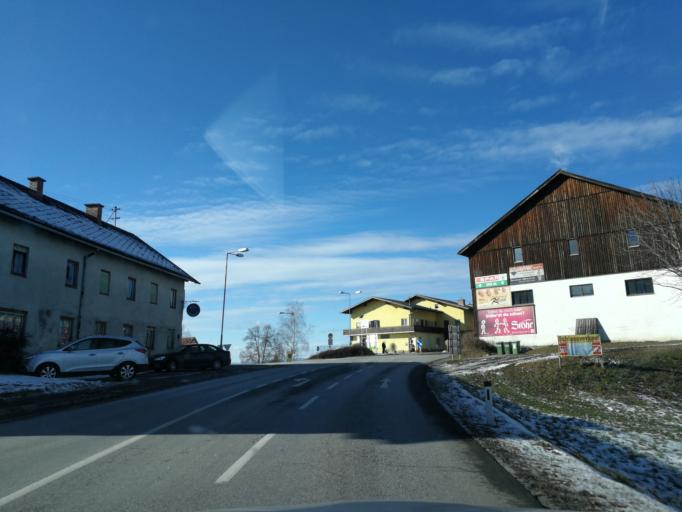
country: AT
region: Styria
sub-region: Politischer Bezirk Graz-Umgebung
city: Nestelbach bei Graz
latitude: 47.0546
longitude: 15.6083
